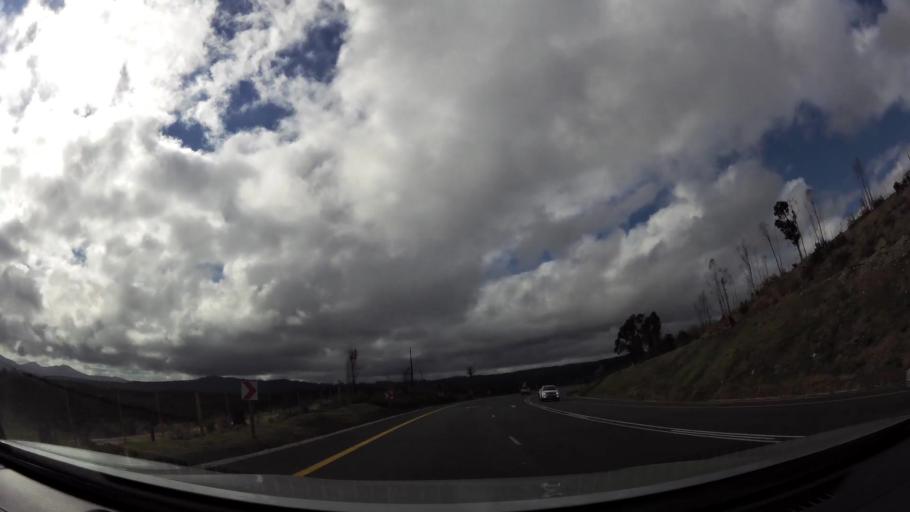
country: ZA
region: Western Cape
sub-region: Eden District Municipality
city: Knysna
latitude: -34.0354
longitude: 23.1242
